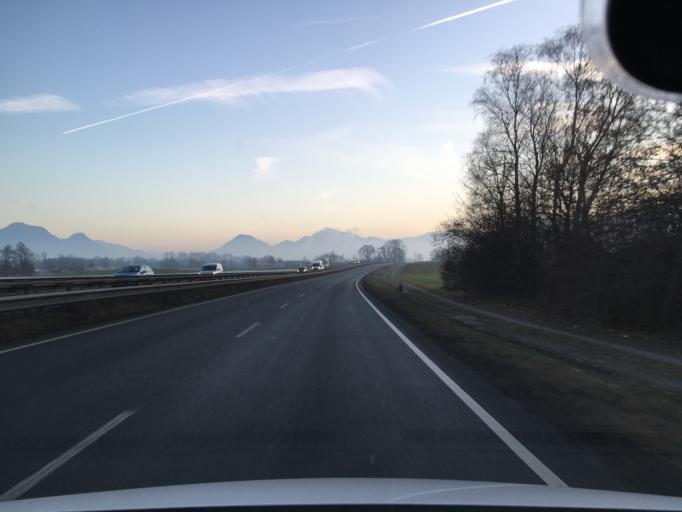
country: DE
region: Bavaria
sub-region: Upper Bavaria
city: Rosenheim
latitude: 47.8261
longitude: 12.1234
